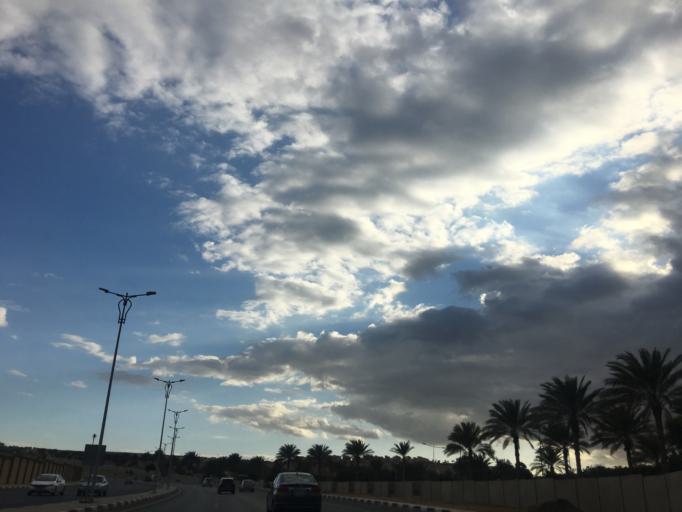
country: EG
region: Muhafazat al Qahirah
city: Cairo
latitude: 30.0368
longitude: 31.3064
